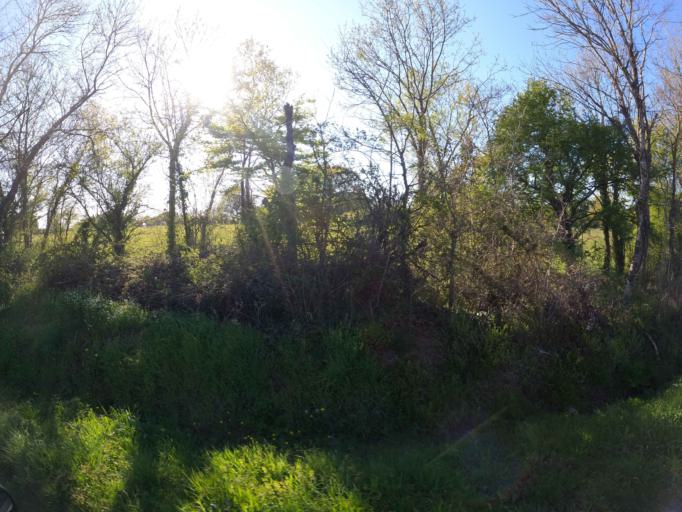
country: FR
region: Pays de la Loire
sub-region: Departement de la Vendee
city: Beaurepaire
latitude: 46.9167
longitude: -1.1228
